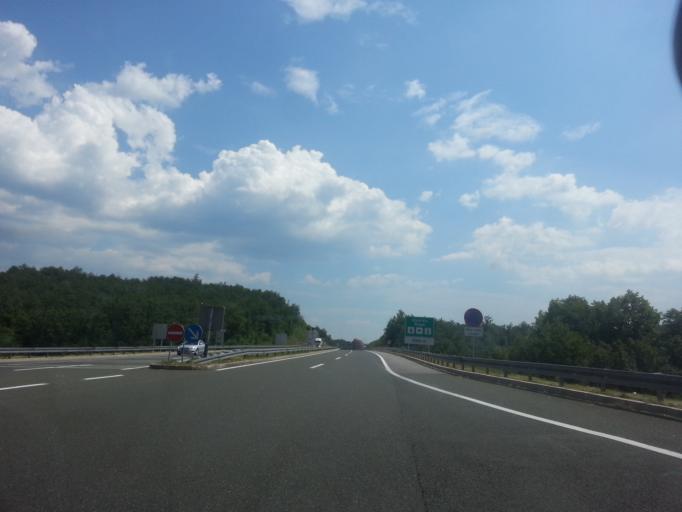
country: HR
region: Primorsko-Goranska
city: Klana
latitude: 45.4553
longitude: 14.2689
